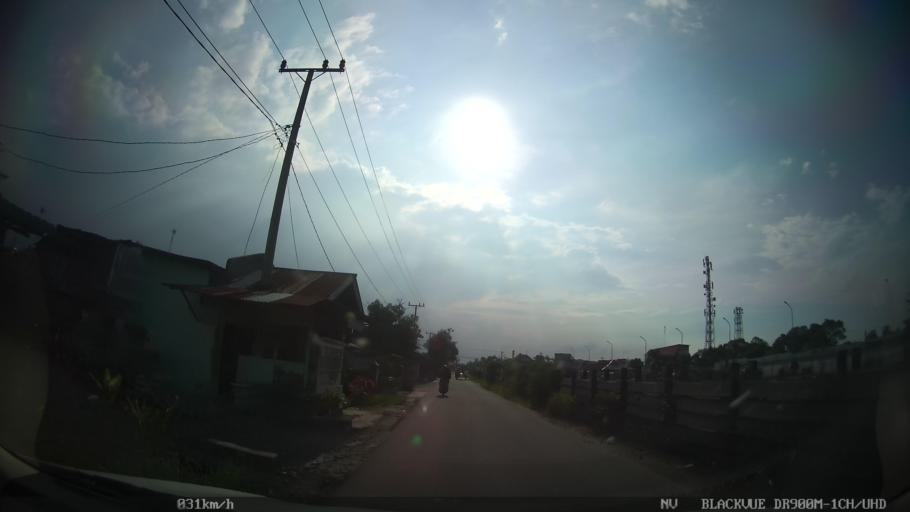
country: ID
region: North Sumatra
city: Medan
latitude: 3.5930
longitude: 98.7562
